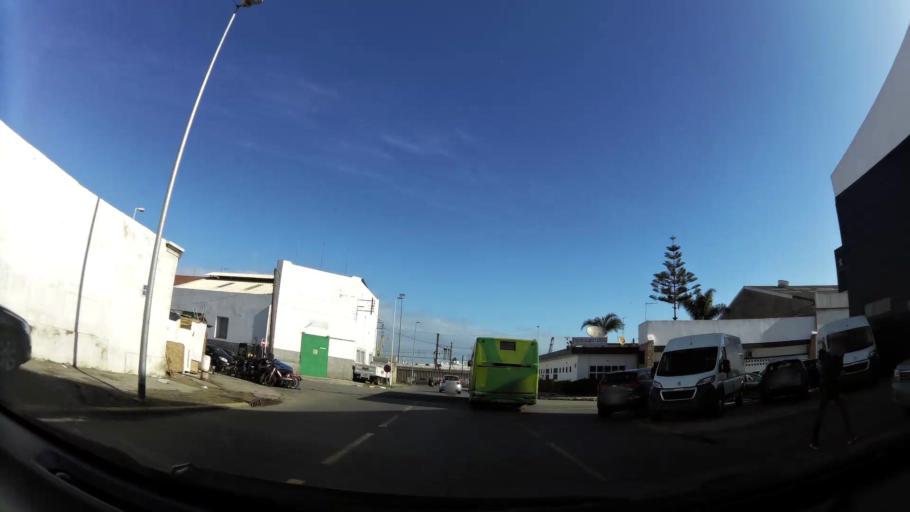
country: MA
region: Grand Casablanca
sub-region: Casablanca
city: Casablanca
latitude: 33.5970
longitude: -7.6061
